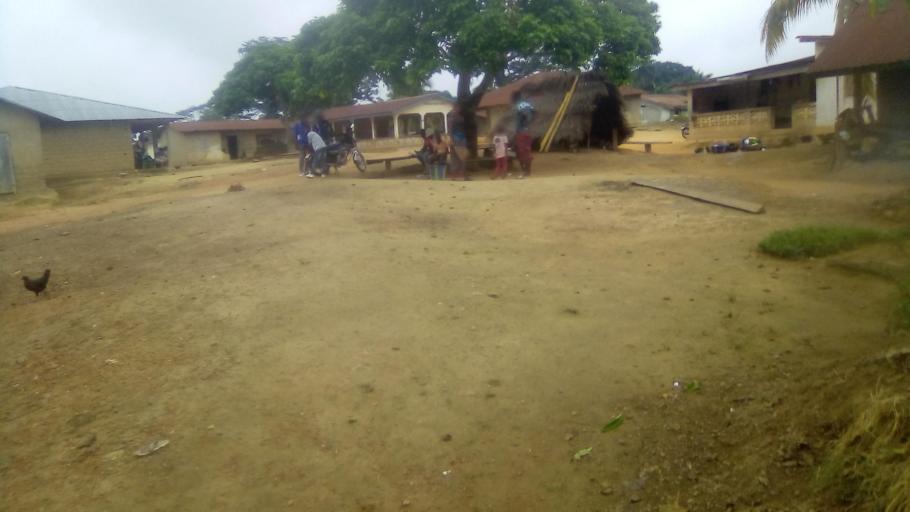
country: SL
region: Eastern Province
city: Kailahun
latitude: 8.2954
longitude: -10.6071
